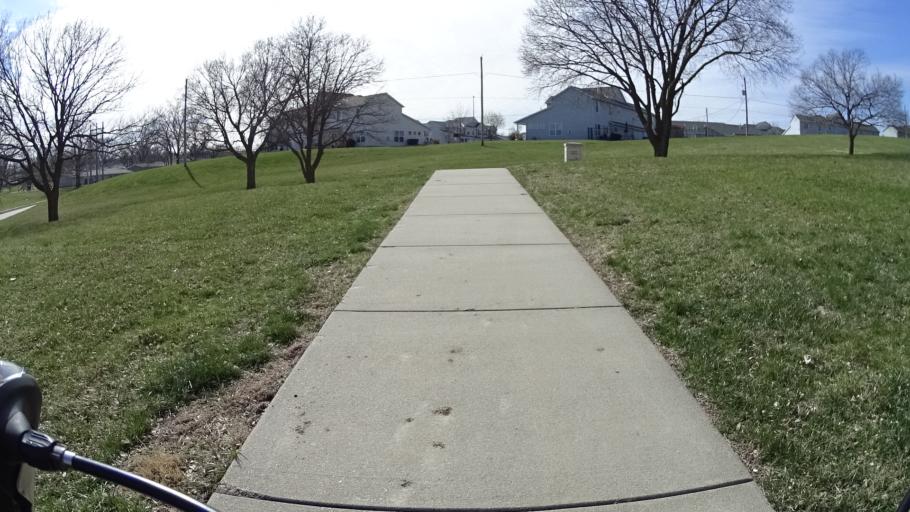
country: US
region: Nebraska
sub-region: Sarpy County
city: Offutt Air Force Base
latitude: 41.1263
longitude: -95.9564
